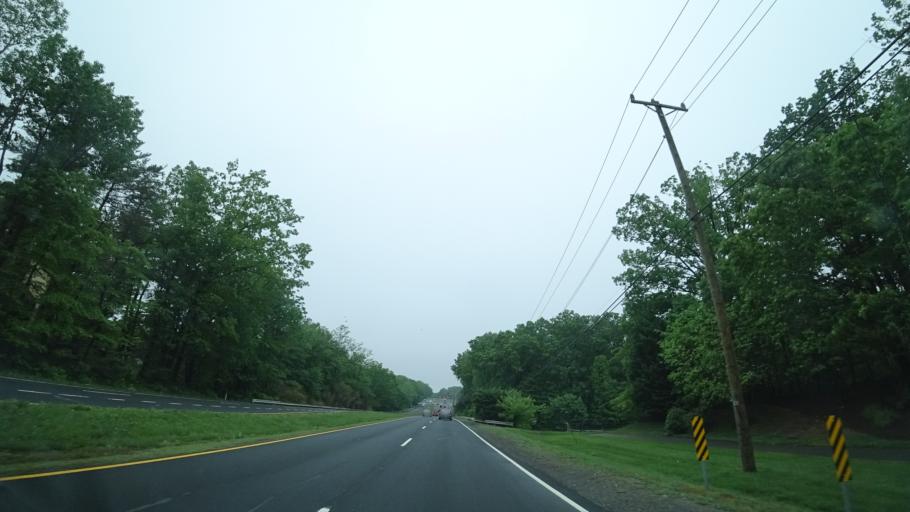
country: US
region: Virginia
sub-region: Fairfax County
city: Reston
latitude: 38.9742
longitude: -77.3291
